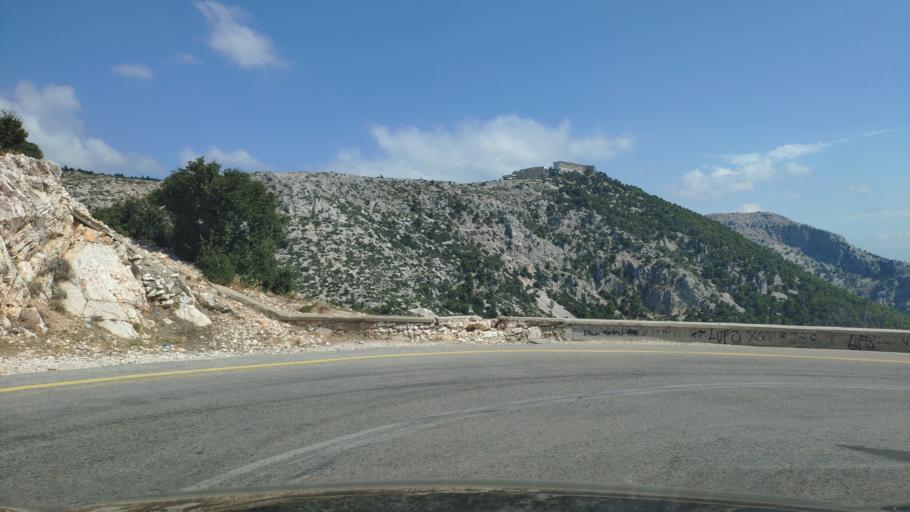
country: GR
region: Attica
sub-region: Nomarchia Anatolikis Attikis
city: Thrakomakedones
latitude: 38.1451
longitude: 23.7273
